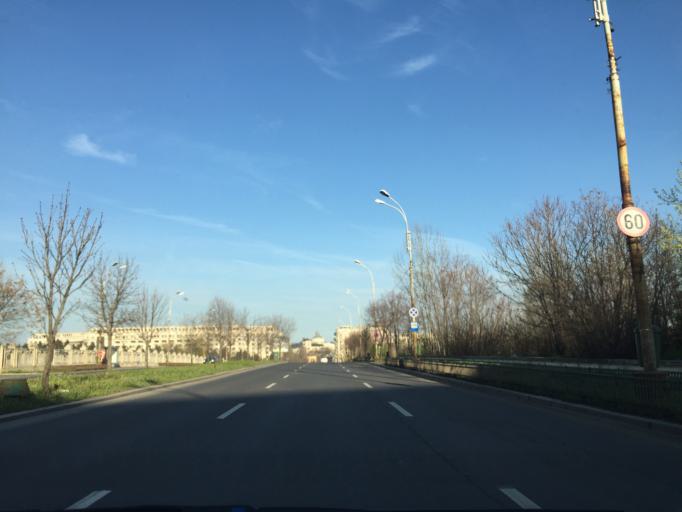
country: RO
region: Bucuresti
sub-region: Municipiul Bucuresti
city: Bucuresti
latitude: 44.4247
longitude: 26.0848
